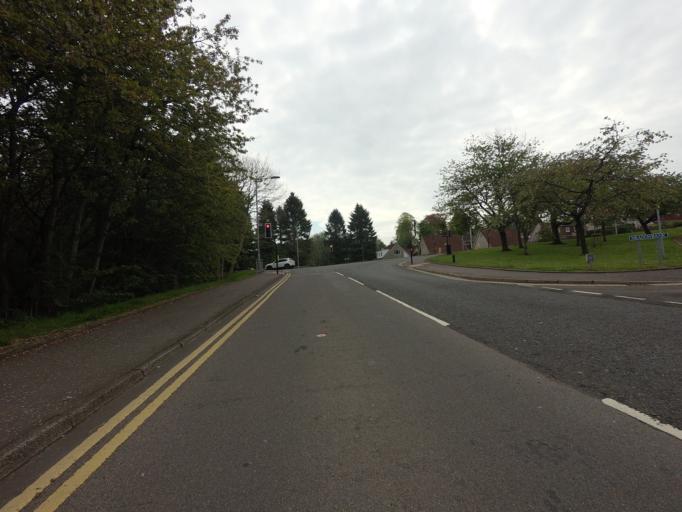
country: GB
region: Scotland
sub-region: Falkirk
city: Polmont
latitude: 55.9867
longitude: -3.7138
